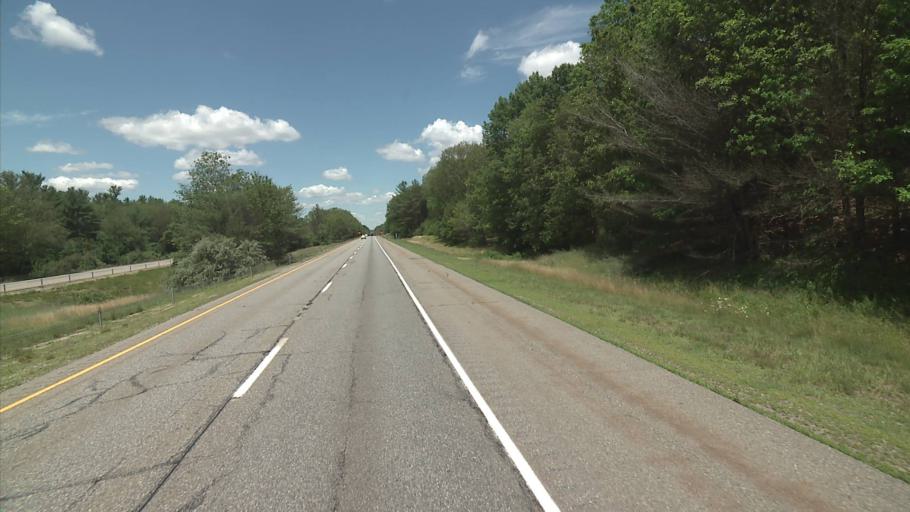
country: US
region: Connecticut
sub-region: Windham County
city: Killingly Center
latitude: 41.8566
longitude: -71.8827
